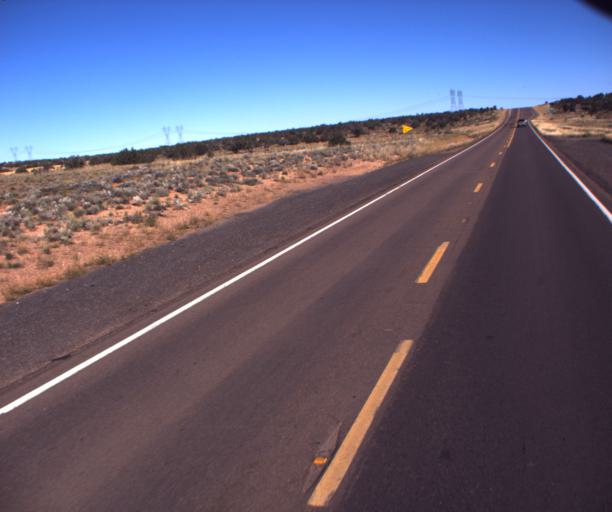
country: US
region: Arizona
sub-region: Navajo County
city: Snowflake
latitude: 34.6253
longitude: -110.0931
